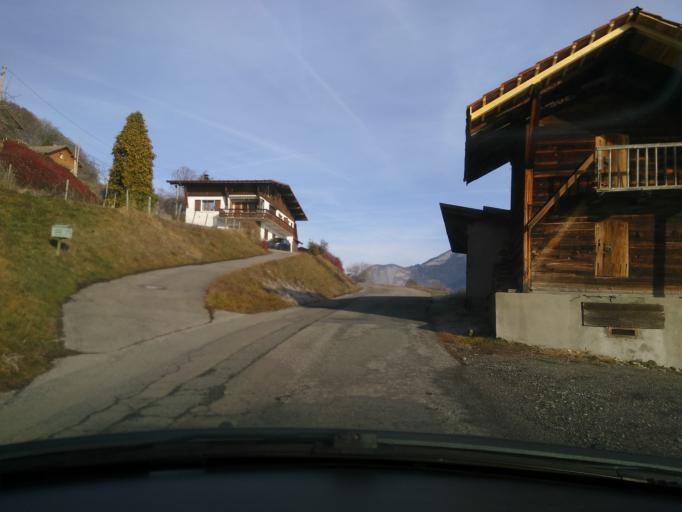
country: FR
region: Rhone-Alpes
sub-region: Departement de la Haute-Savoie
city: Sallanches
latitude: 45.9480
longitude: 6.6210
